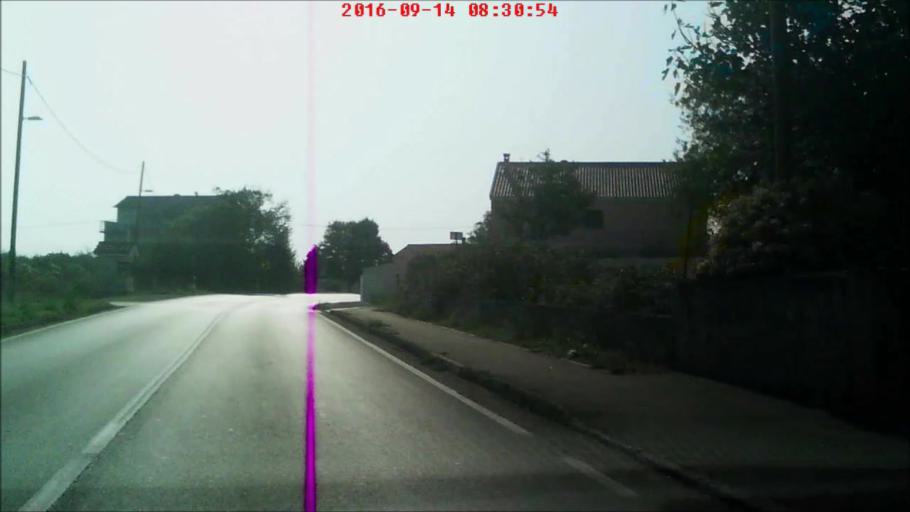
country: HR
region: Zadarska
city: Zadar
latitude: 44.1702
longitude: 15.2936
